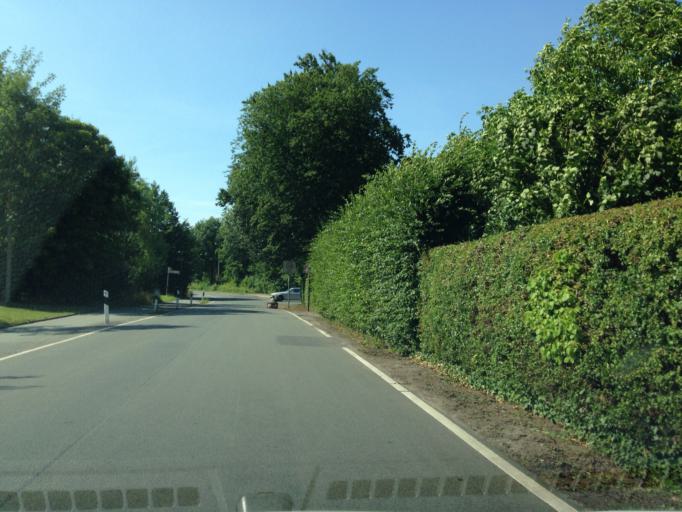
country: DE
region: North Rhine-Westphalia
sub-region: Regierungsbezirk Munster
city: Muenster
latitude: 51.9640
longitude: 7.5744
